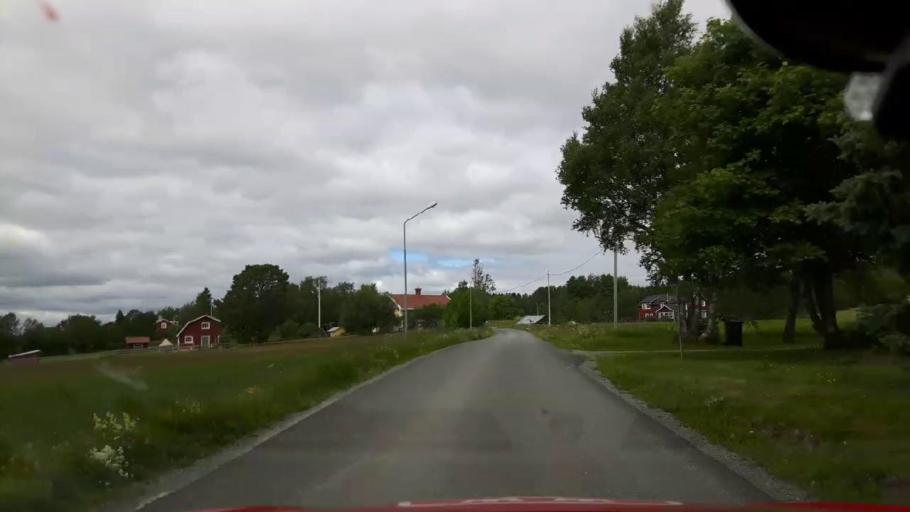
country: SE
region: Jaemtland
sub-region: OEstersunds Kommun
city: Brunflo
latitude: 63.0739
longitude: 14.8863
